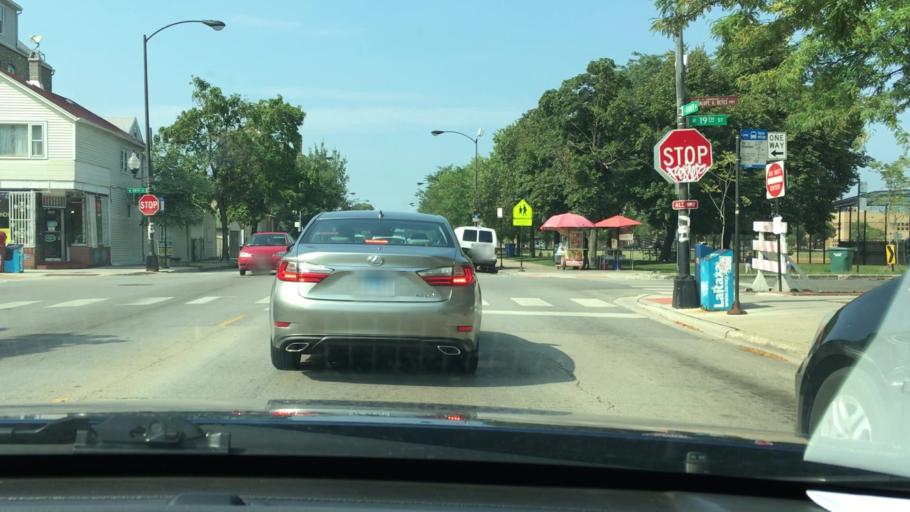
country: US
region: Illinois
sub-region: Cook County
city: Chicago
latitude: 41.8556
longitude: -87.6759
